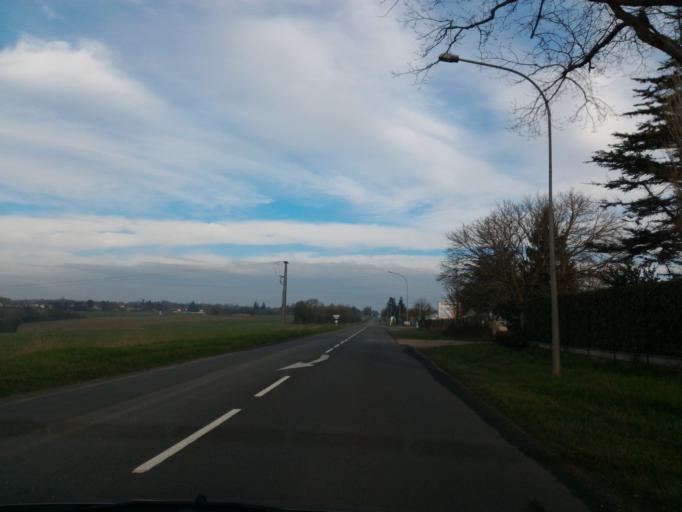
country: FR
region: Poitou-Charentes
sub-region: Departement de la Charente
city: Ruffec
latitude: 46.0391
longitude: 0.1974
